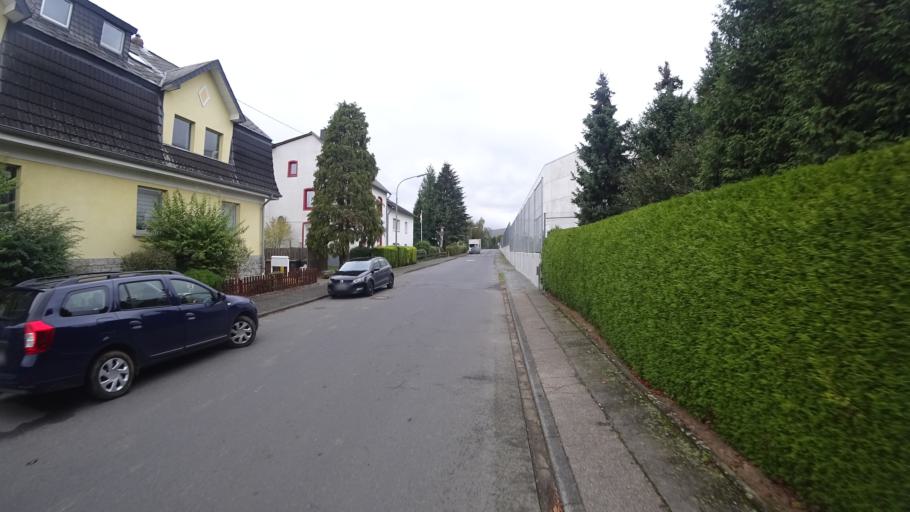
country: DE
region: Rheinland-Pfalz
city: Selters
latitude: 50.5345
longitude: 7.7538
